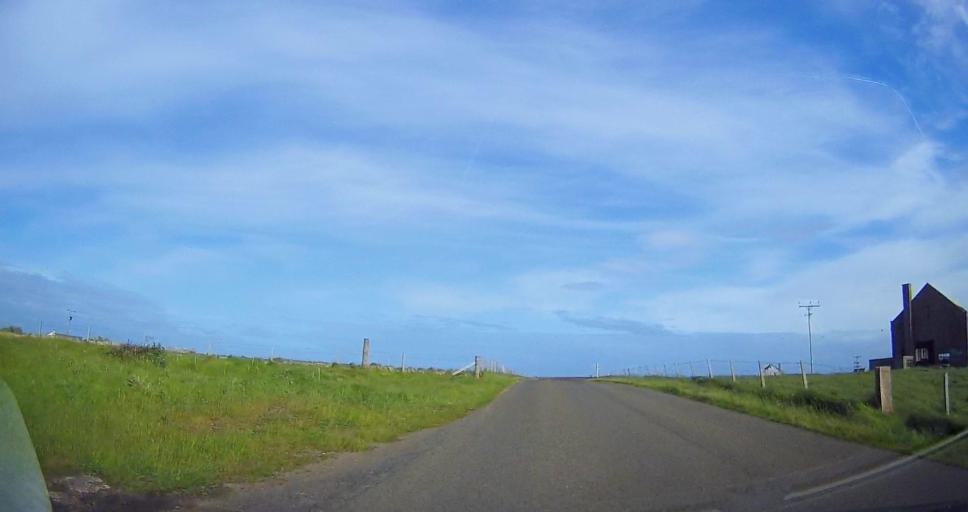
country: GB
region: Scotland
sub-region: Orkney Islands
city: Stromness
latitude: 58.8235
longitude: -3.2087
